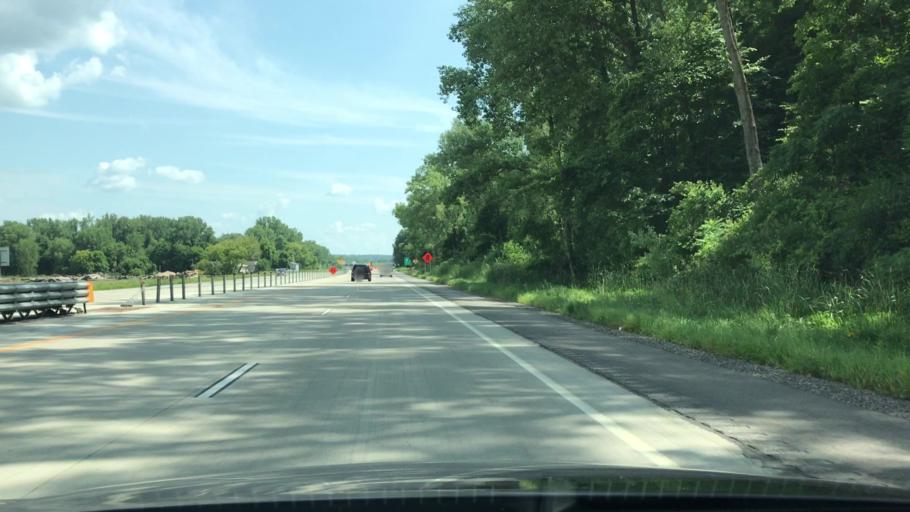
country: US
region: Minnesota
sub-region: Nicollet County
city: North Mankato
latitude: 44.2070
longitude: -94.0249
